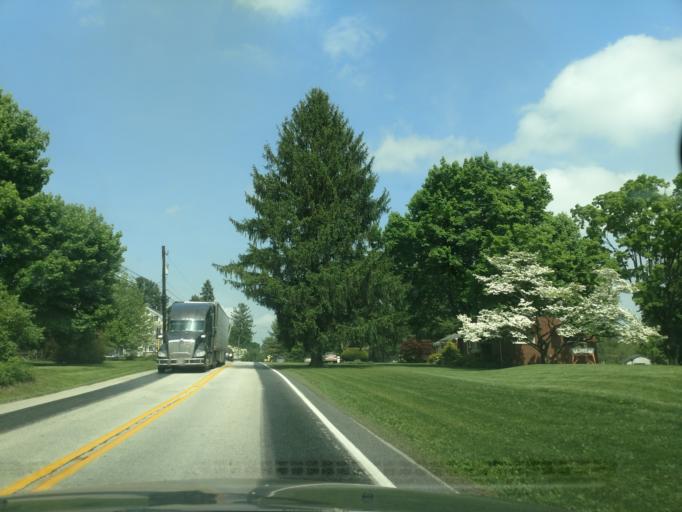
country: US
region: Pennsylvania
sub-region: Chester County
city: Kenilworth
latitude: 40.1766
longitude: -75.6356
